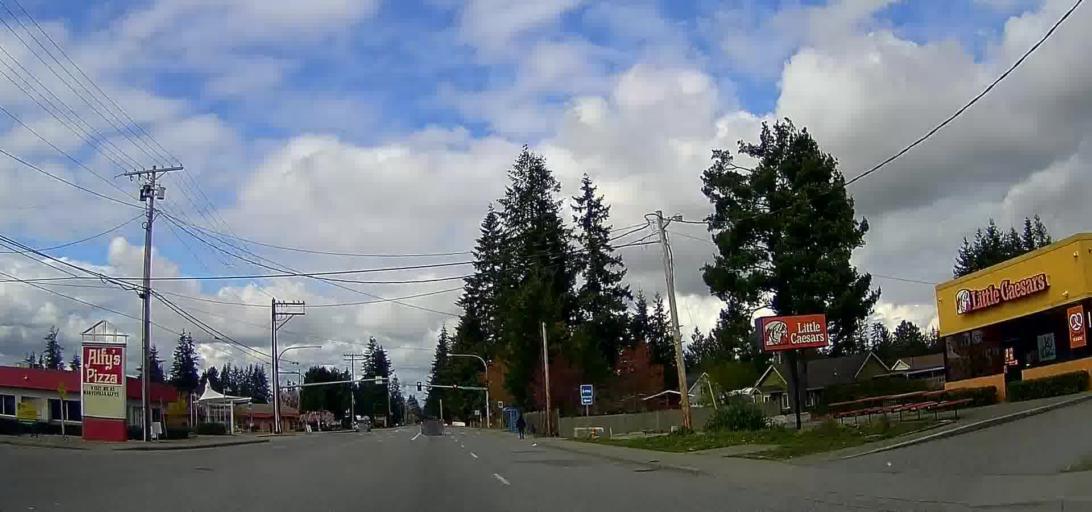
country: US
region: Washington
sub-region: Snohomish County
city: Smokey Point
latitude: 48.1539
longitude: -122.1829
